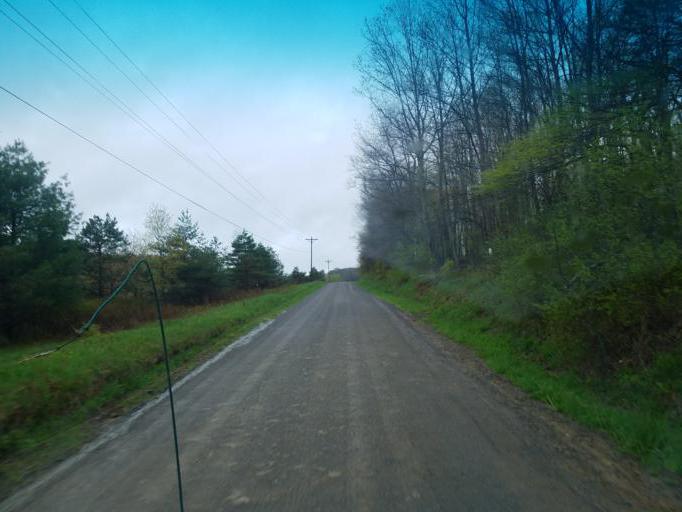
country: US
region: Pennsylvania
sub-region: Tioga County
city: Westfield
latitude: 41.9808
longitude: -77.6893
